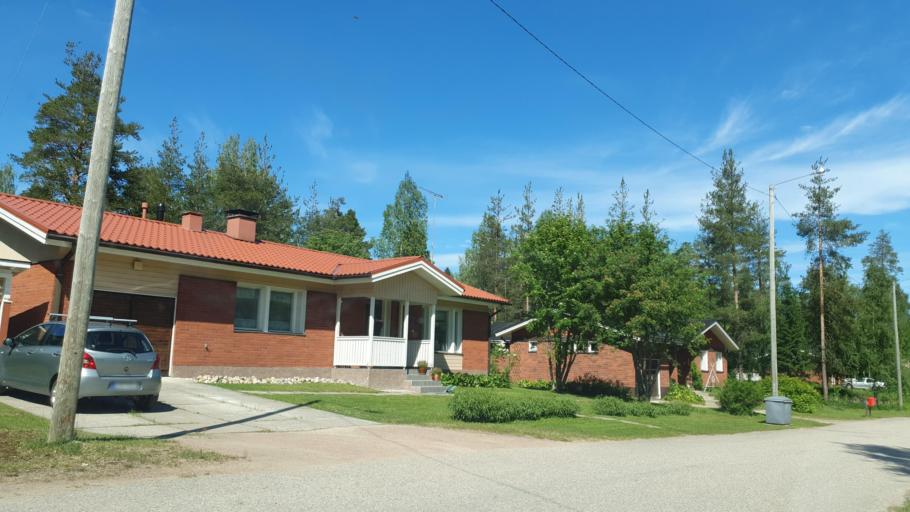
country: FI
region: Kainuu
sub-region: Kehys-Kainuu
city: Hyrynsalmi
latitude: 64.6813
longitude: 28.4650
